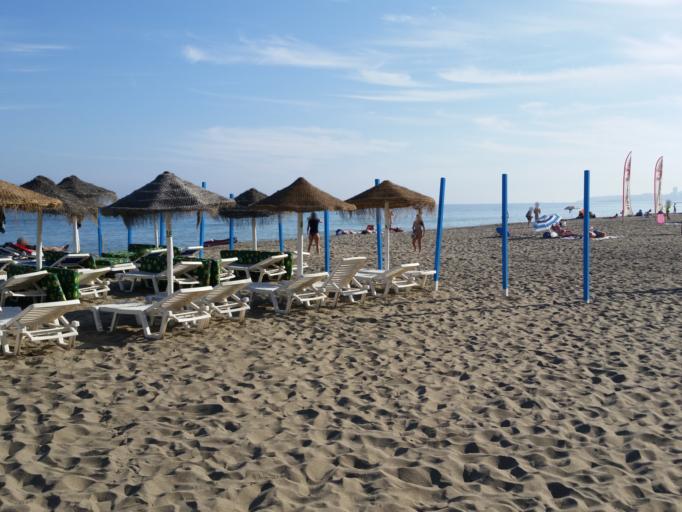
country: ES
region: Andalusia
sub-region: Provincia de Malaga
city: Benalmadena
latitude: 36.5699
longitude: -4.5923
